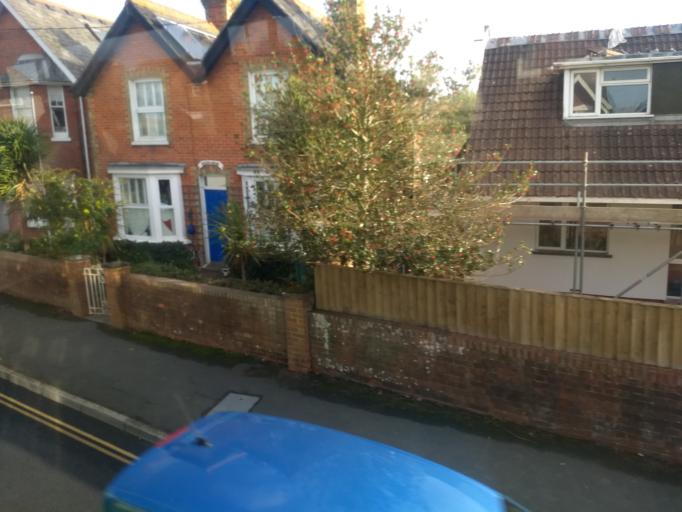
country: GB
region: England
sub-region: Isle of Wight
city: Yarmouth
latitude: 50.7049
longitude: -1.4971
